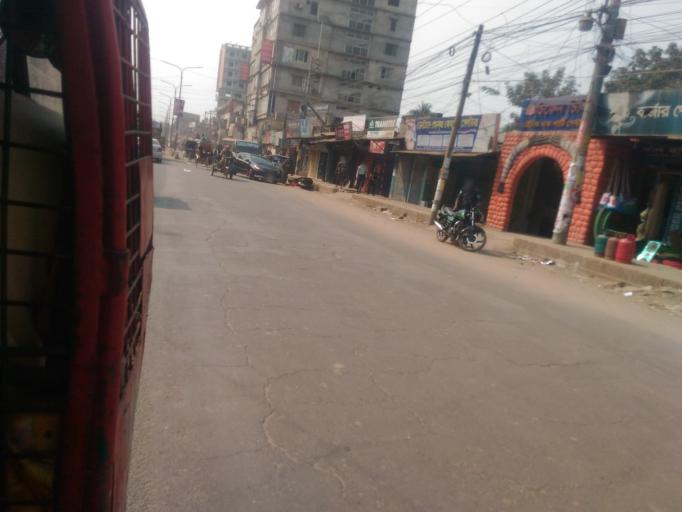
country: BD
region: Dhaka
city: Tungi
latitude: 23.9999
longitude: 90.4240
